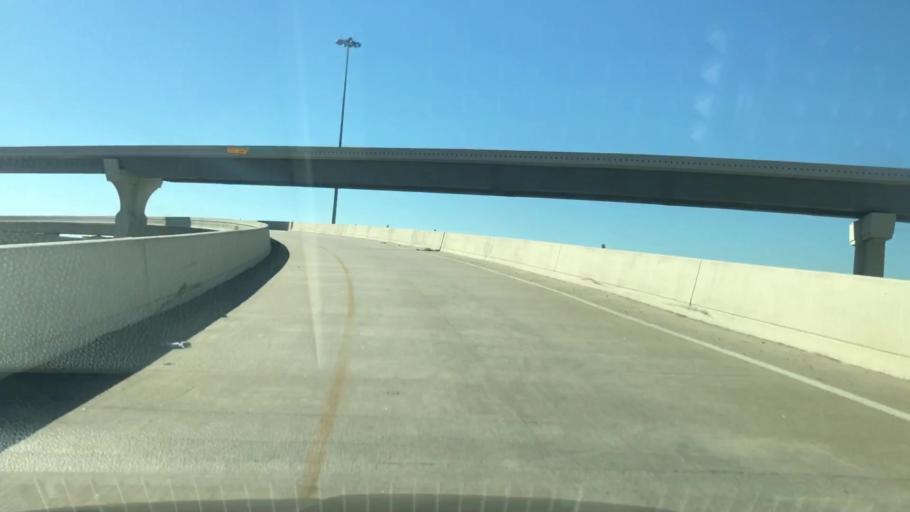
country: US
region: Texas
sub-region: Harris County
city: Cypress
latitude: 29.9977
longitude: -95.7680
